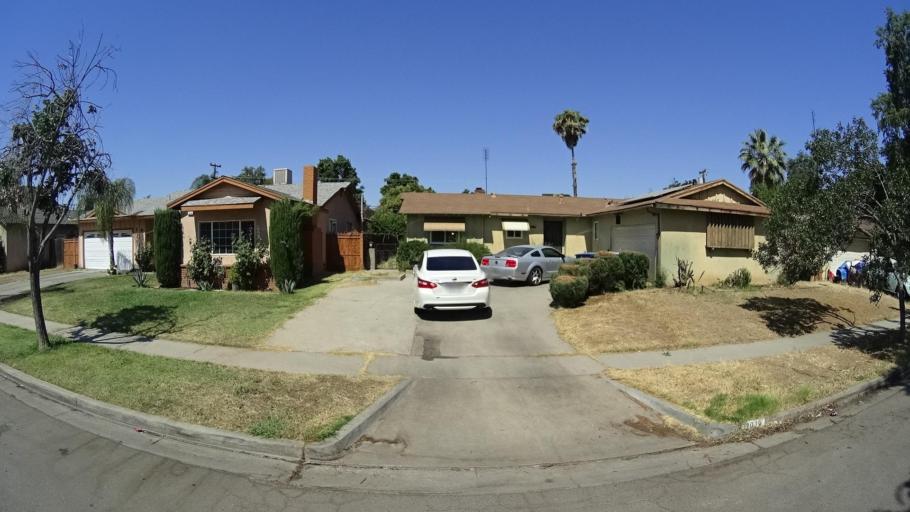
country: US
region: California
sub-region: Fresno County
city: Fresno
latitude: 36.7229
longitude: -119.7408
